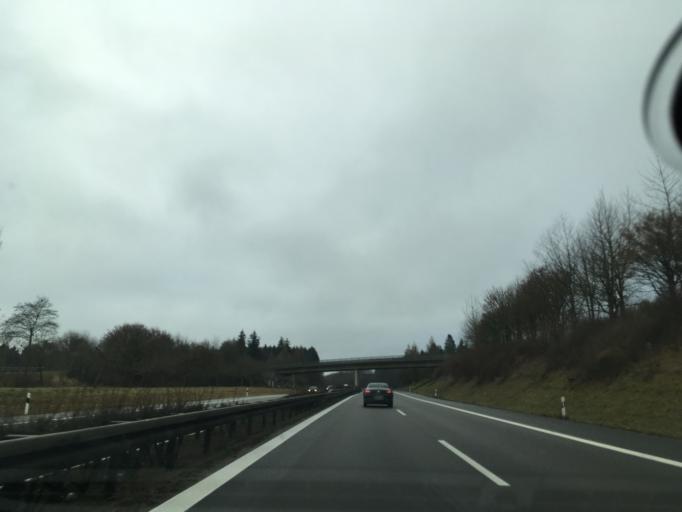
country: DE
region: Bavaria
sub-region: Swabia
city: Mindelheim
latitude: 48.0276
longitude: 10.4679
